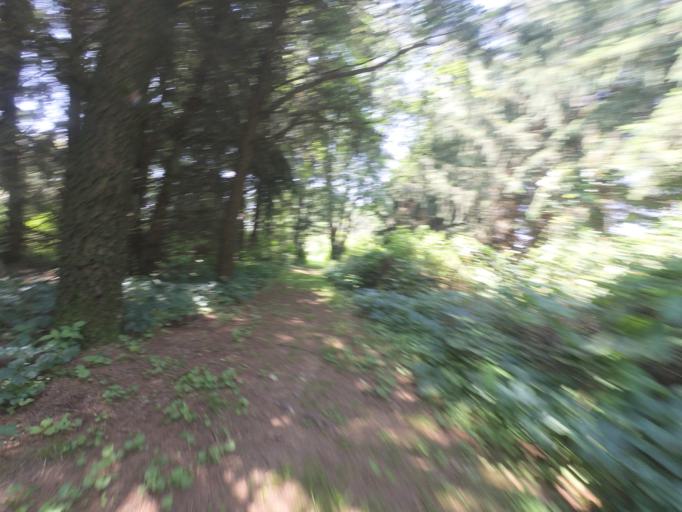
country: US
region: Pennsylvania
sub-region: Centre County
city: Houserville
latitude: 40.8502
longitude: -77.8700
